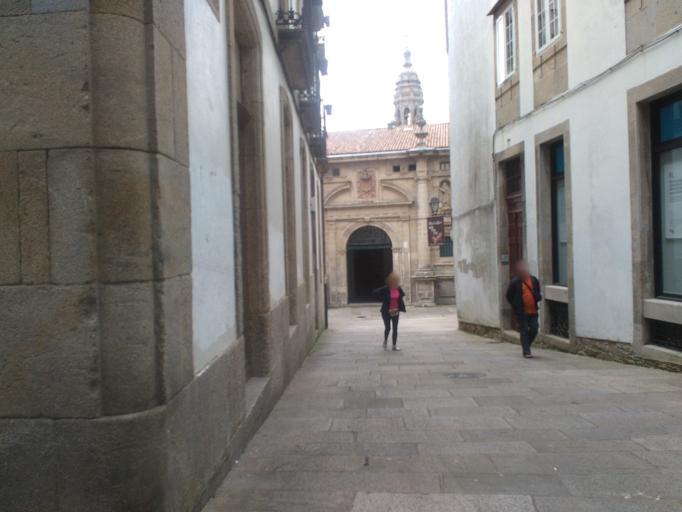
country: ES
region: Galicia
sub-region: Provincia da Coruna
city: Santiago de Compostela
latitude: 42.8806
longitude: -8.5424
